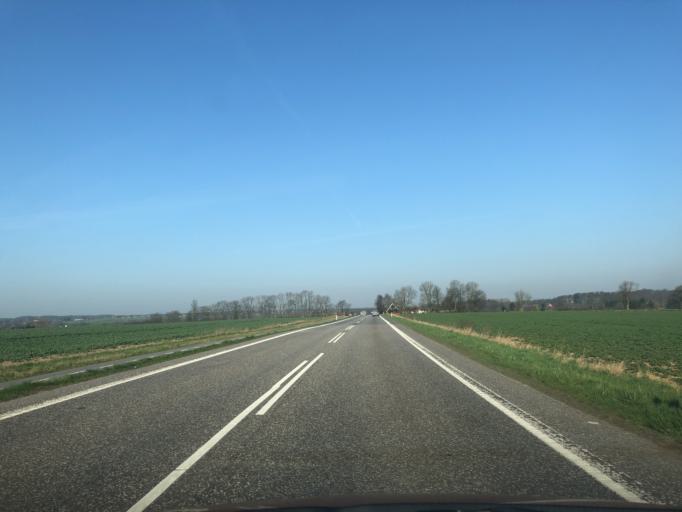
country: DK
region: Zealand
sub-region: Faxe Kommune
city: Fakse
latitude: 55.2544
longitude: 12.0835
